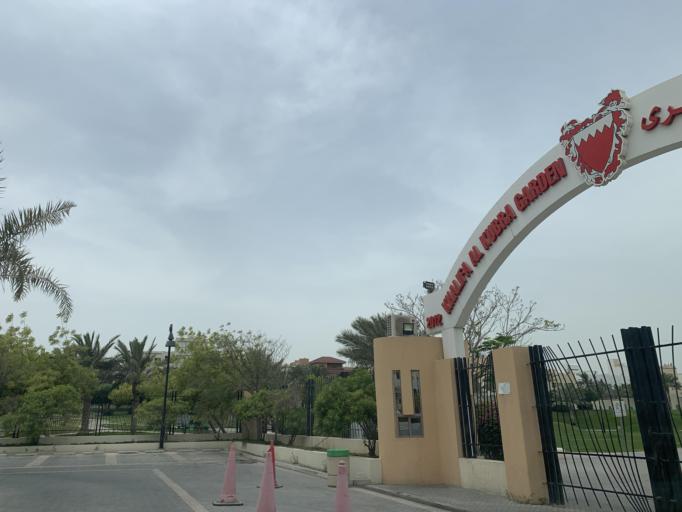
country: BH
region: Northern
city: Ar Rifa'
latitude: 26.1343
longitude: 50.5665
